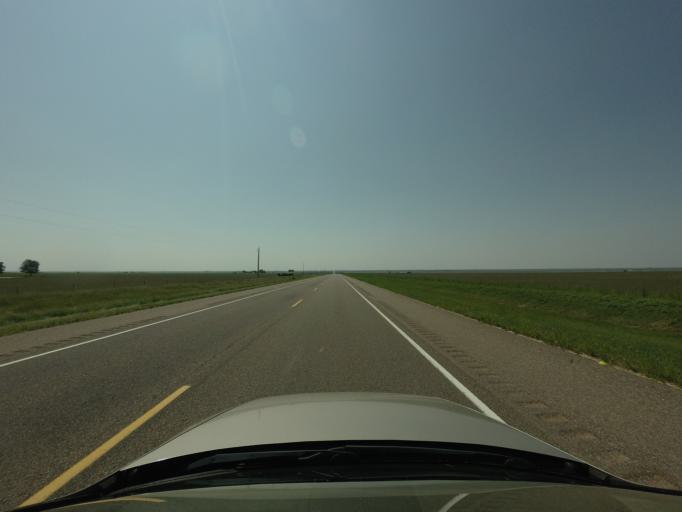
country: US
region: New Mexico
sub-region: Curry County
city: Clovis
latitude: 34.5584
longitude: -103.1966
